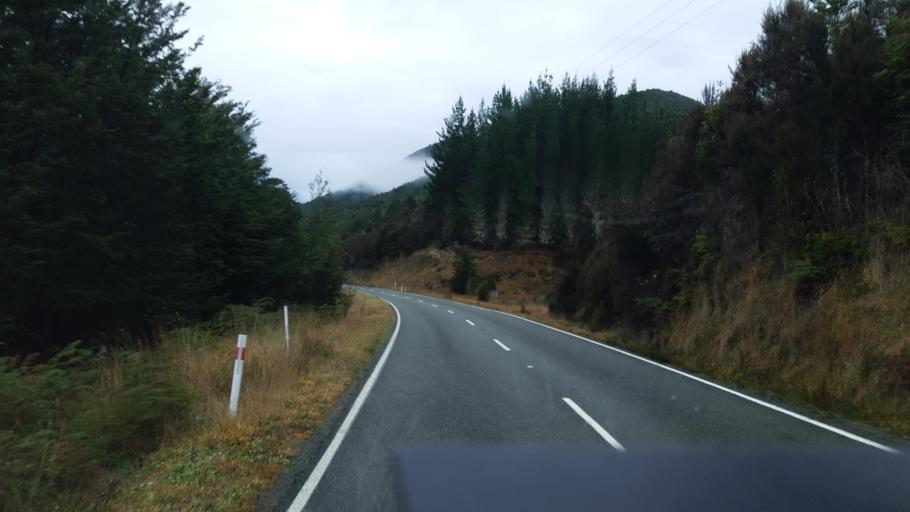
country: NZ
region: Tasman
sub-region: Tasman District
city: Wakefield
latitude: -41.7534
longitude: 172.8970
